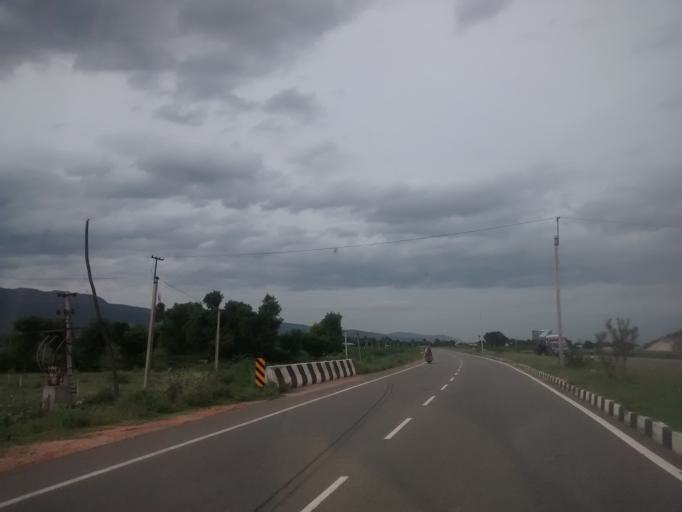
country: IN
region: Andhra Pradesh
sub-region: Chittoor
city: Narasingapuram
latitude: 13.5991
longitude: 79.3590
